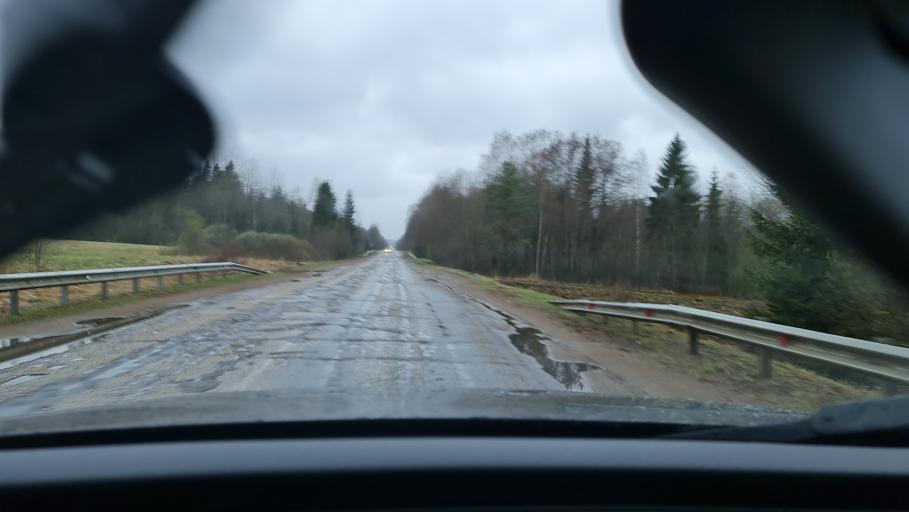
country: RU
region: Novgorod
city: Valday
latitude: 58.0356
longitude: 32.8752
